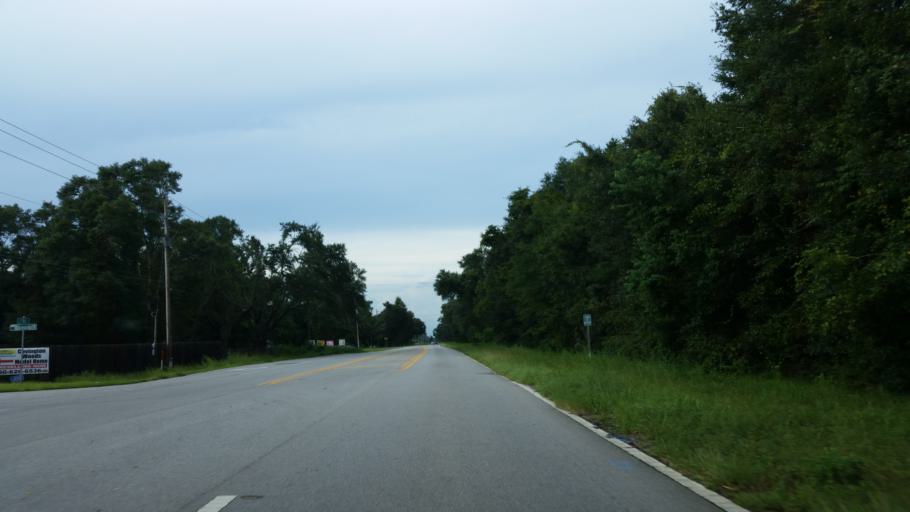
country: US
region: Florida
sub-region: Santa Rosa County
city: Pace
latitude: 30.5823
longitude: -87.1117
